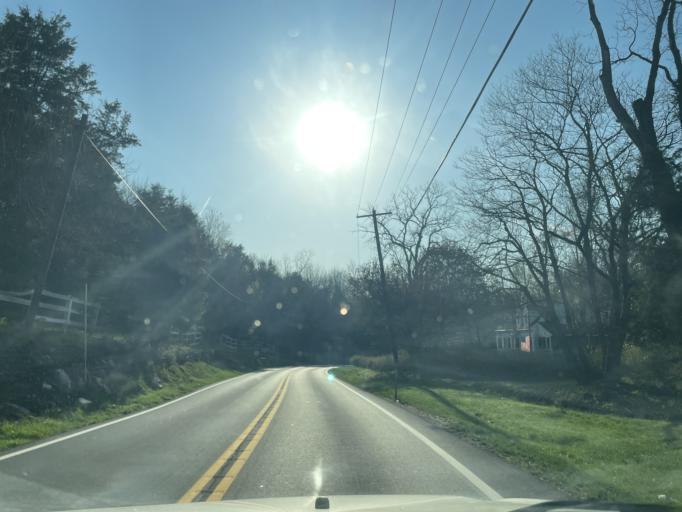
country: US
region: Maryland
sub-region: Washington County
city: Saint James
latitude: 39.5420
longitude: -77.7141
